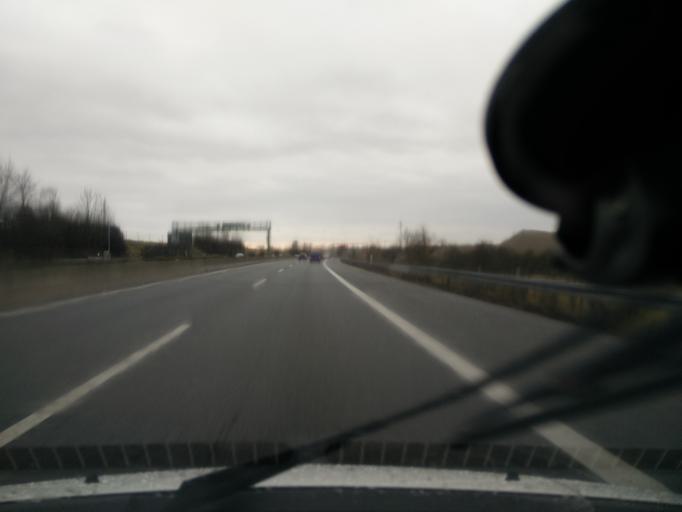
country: DE
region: Bavaria
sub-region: Upper Bavaria
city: Karlsfeld
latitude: 48.1938
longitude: 11.4373
